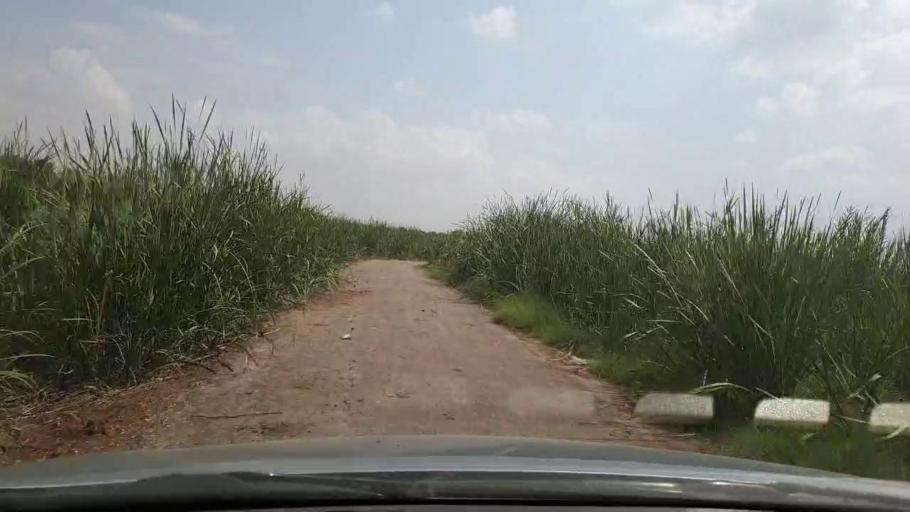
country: PK
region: Sindh
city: Khairpur
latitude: 27.4624
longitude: 68.7772
